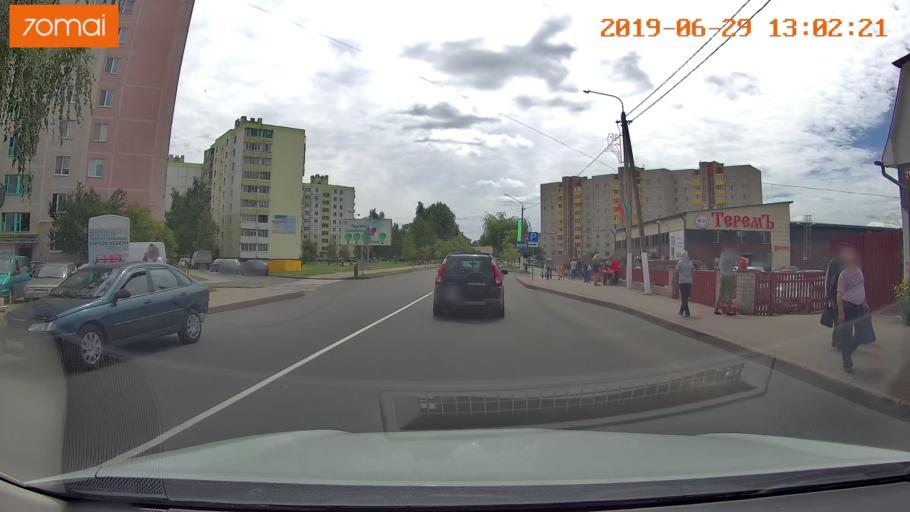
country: BY
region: Minsk
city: Slutsk
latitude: 53.0352
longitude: 27.5599
